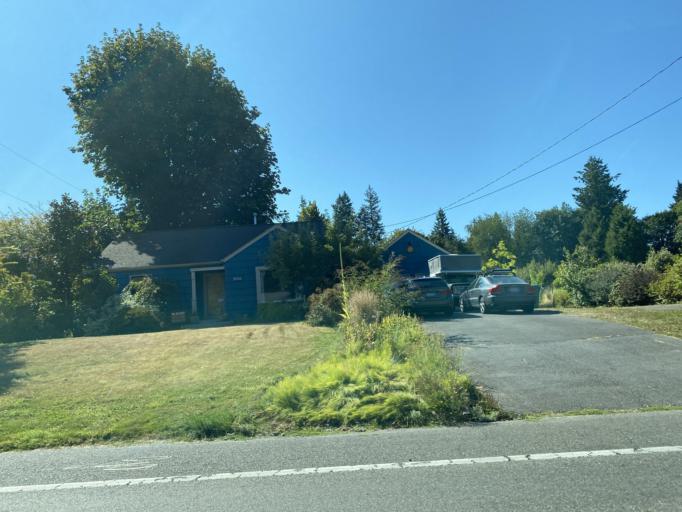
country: US
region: Washington
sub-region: Thurston County
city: Olympia
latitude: 47.0295
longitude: -122.8791
